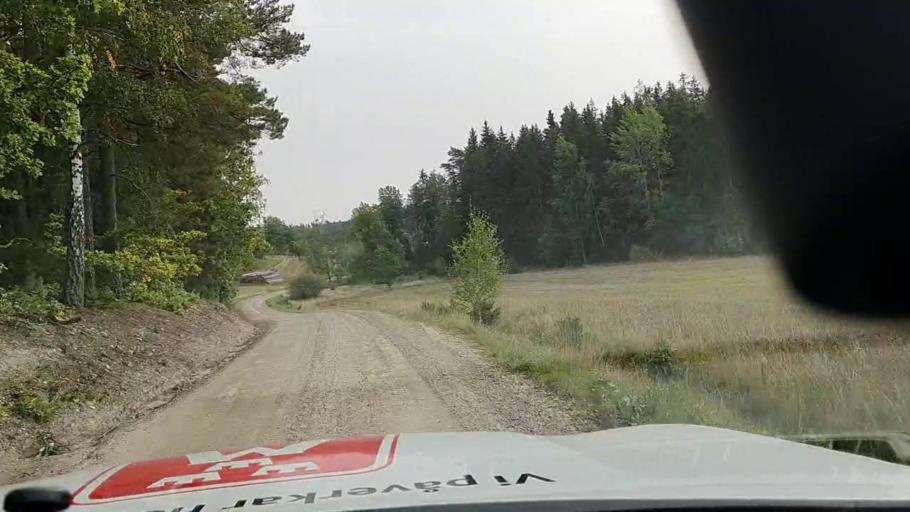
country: SE
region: Soedermanland
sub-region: Nykopings Kommun
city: Nykoping
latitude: 58.8995
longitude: 16.9845
